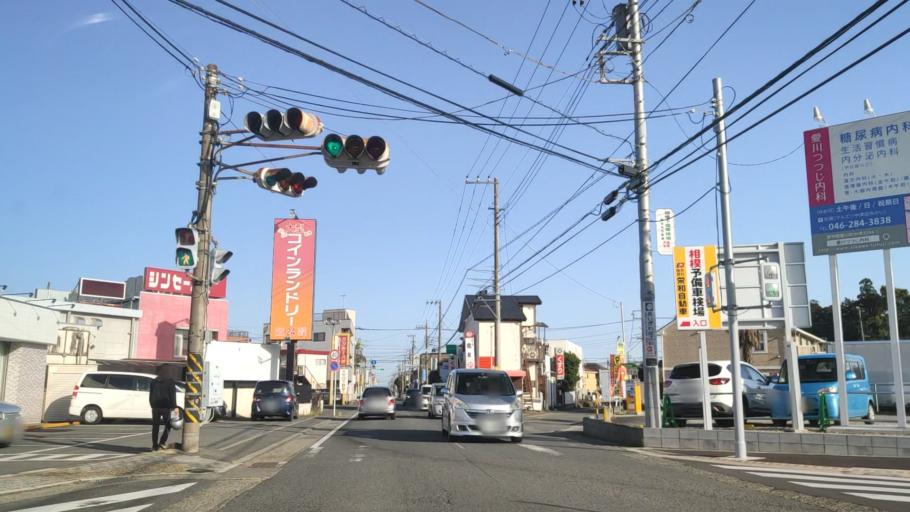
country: JP
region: Kanagawa
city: Zama
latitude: 35.5041
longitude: 139.3510
